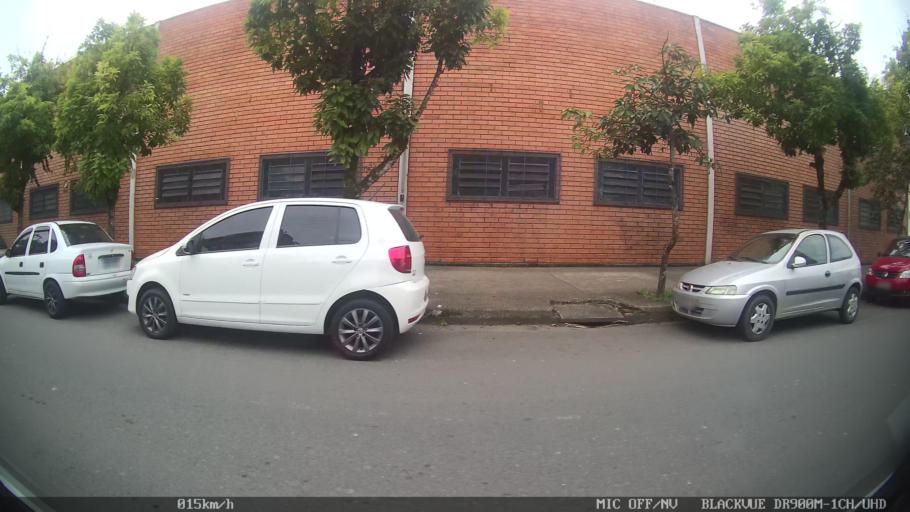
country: BR
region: Santa Catarina
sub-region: Joinville
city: Joinville
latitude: -26.3152
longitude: -48.8394
